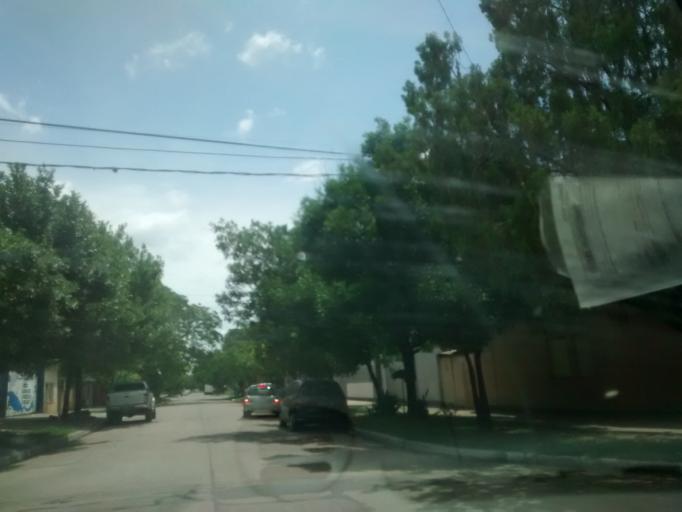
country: AR
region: Chaco
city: Resistencia
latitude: -27.4426
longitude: -58.9892
